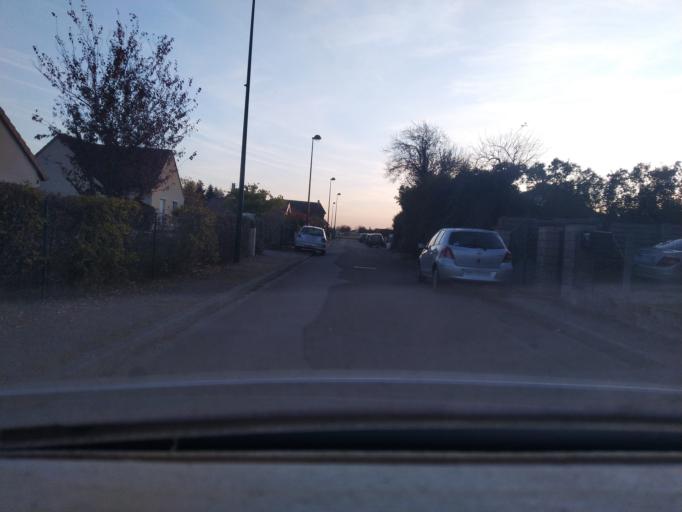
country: FR
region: Haute-Normandie
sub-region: Departement de la Seine-Maritime
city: Yainville
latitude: 49.4491
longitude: 0.8281
